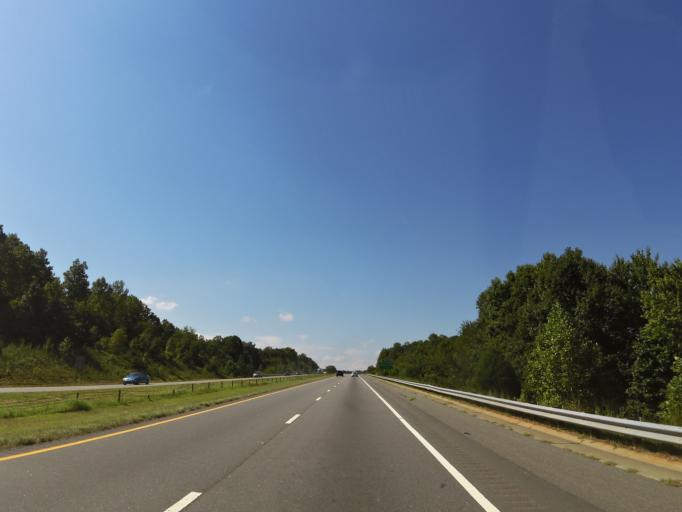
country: US
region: North Carolina
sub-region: Catawba County
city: Mountain View
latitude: 35.6693
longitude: -81.3316
